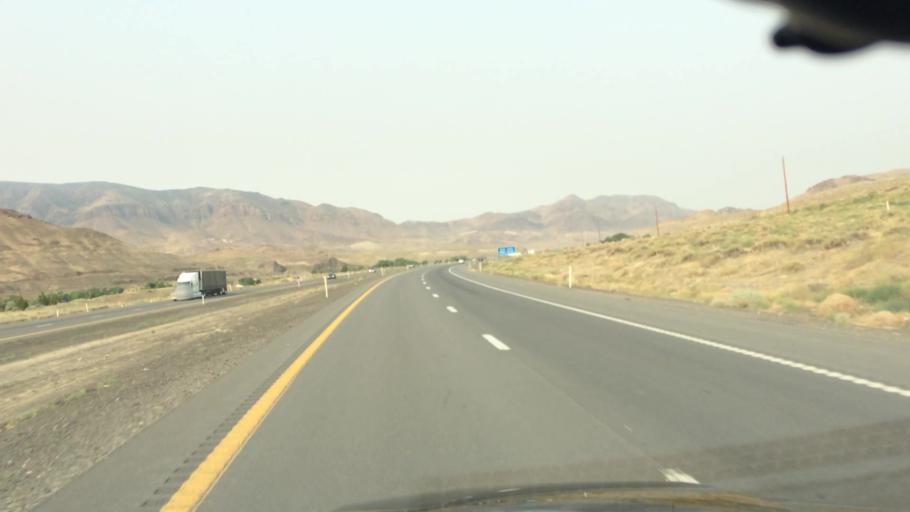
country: US
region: Nevada
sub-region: Lyon County
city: Fernley
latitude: 39.6072
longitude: -119.3240
